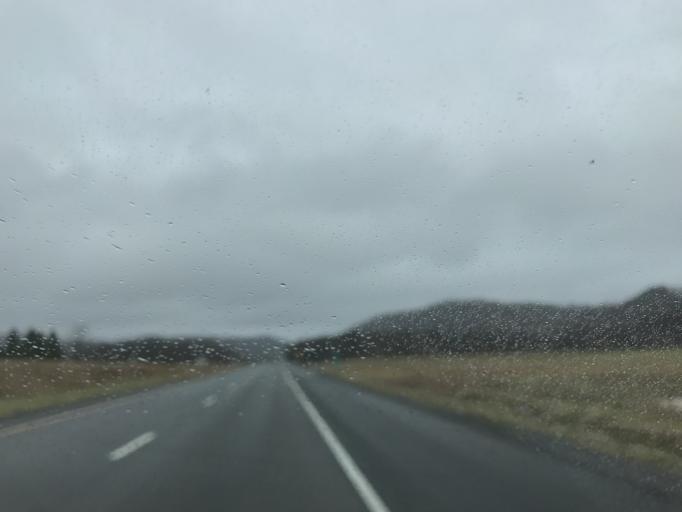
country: US
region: West Virginia
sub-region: Greenbrier County
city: Rainelle
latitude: 37.9035
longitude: -80.6331
